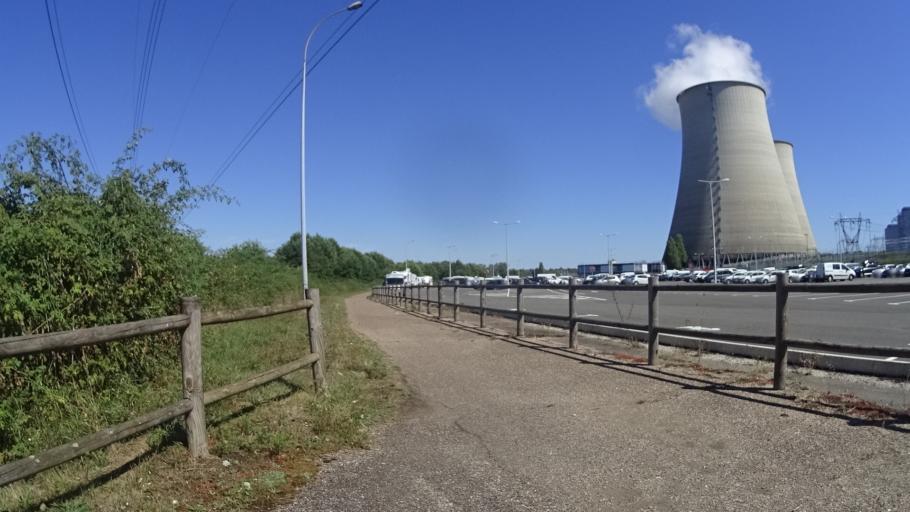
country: FR
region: Centre
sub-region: Departement du Cher
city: Belleville-sur-Loire
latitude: 47.5084
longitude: 2.8677
